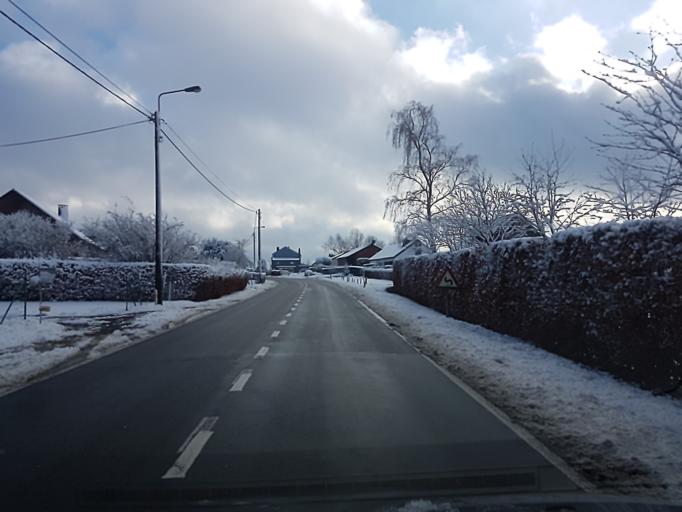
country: BE
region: Wallonia
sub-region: Province de Liege
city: Jalhay
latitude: 50.5659
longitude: 5.9369
